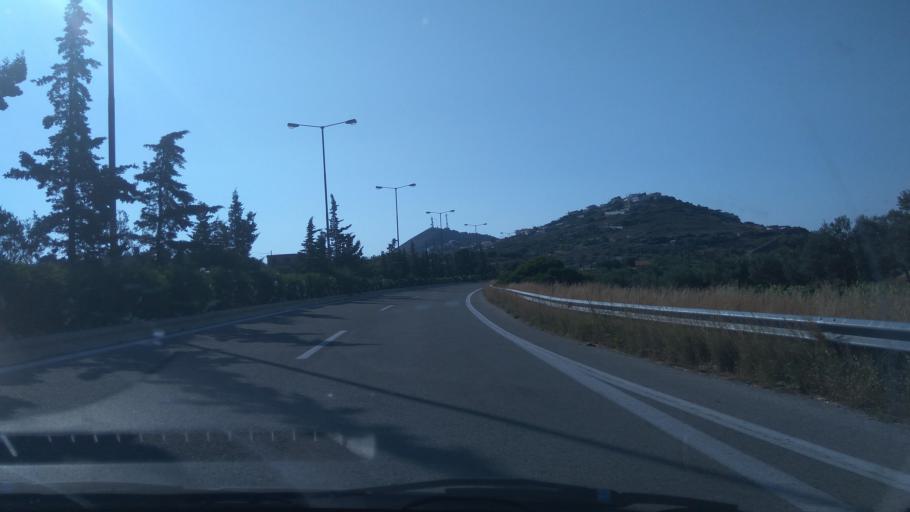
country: GR
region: Attica
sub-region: Nomarchia Anatolikis Attikis
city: Keratea
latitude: 37.8030
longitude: 24.0455
